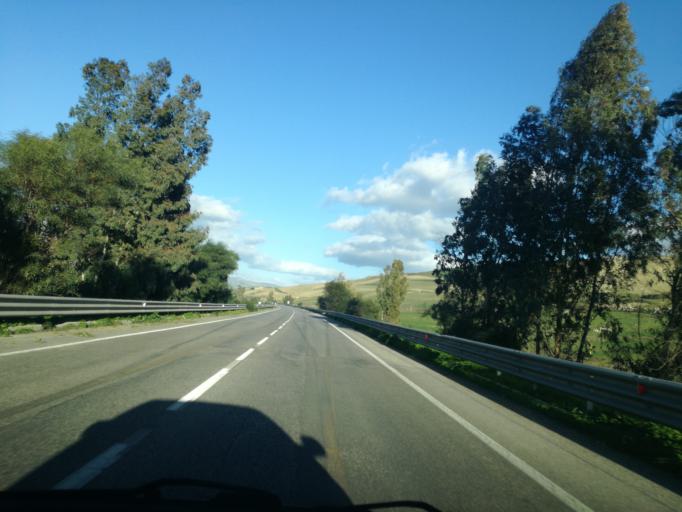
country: IT
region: Sicily
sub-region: Enna
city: Pietraperzia
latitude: 37.4351
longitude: 14.0905
